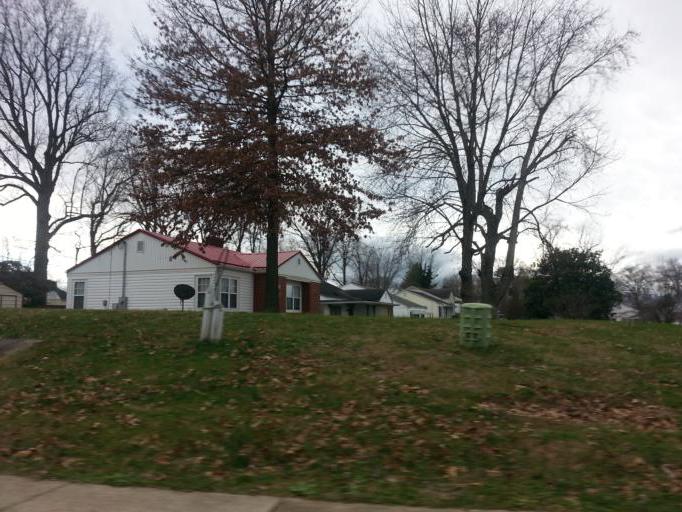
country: US
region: Tennessee
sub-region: Washington County
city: Johnson City
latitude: 36.3123
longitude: -82.3663
